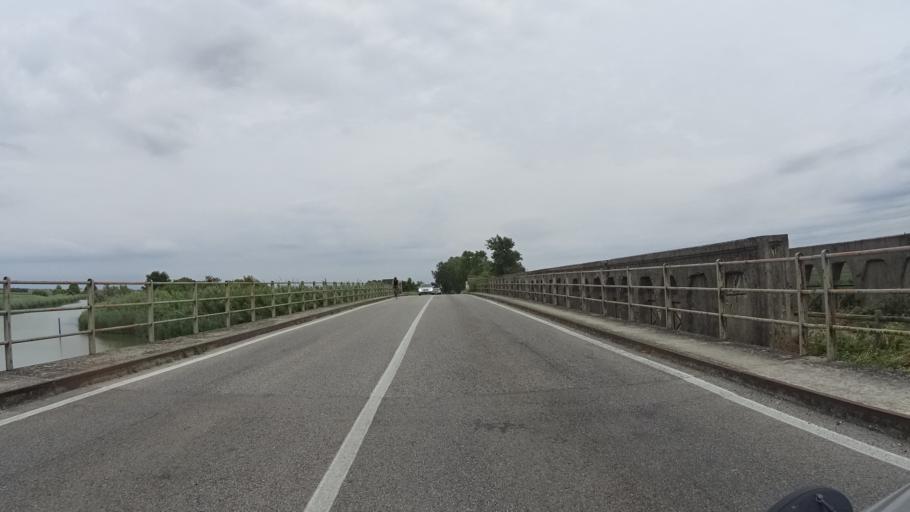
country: IT
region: Veneto
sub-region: Provincia di Venezia
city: La Salute di Livenza
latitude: 45.6894
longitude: 12.8448
